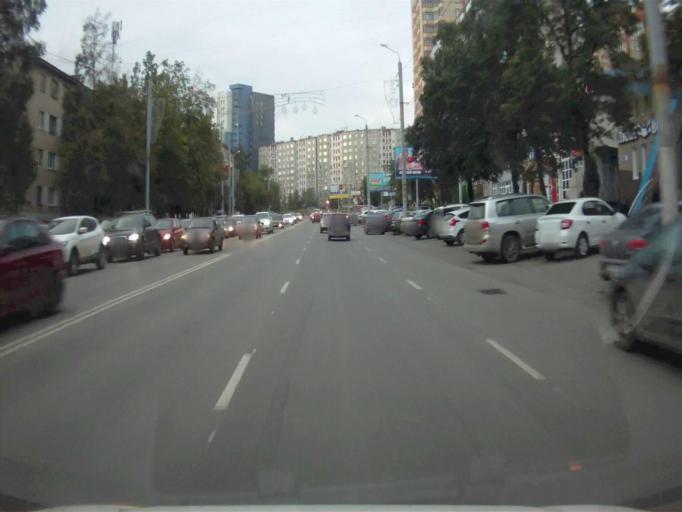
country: RU
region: Chelyabinsk
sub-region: Gorod Chelyabinsk
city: Chelyabinsk
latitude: 55.1552
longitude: 61.3815
